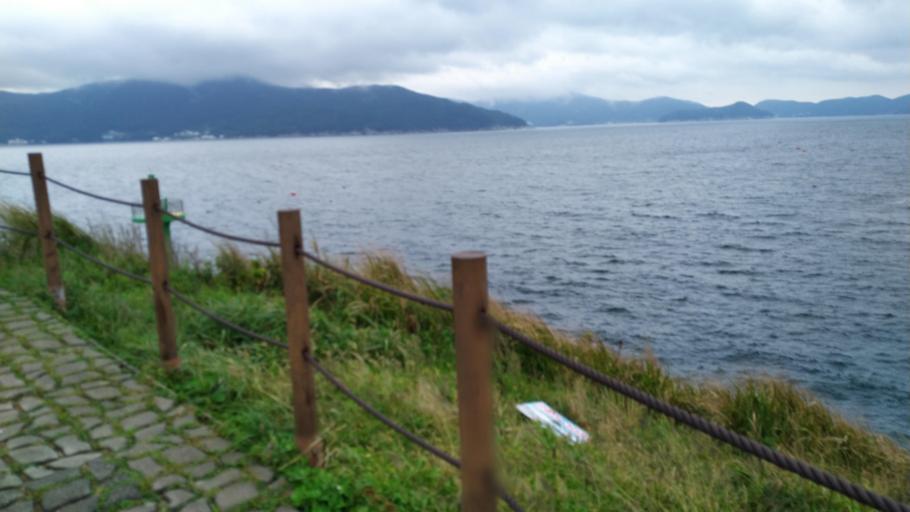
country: KR
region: Gyeongsangnam-do
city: Kyosai
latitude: 34.7447
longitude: 128.6633
